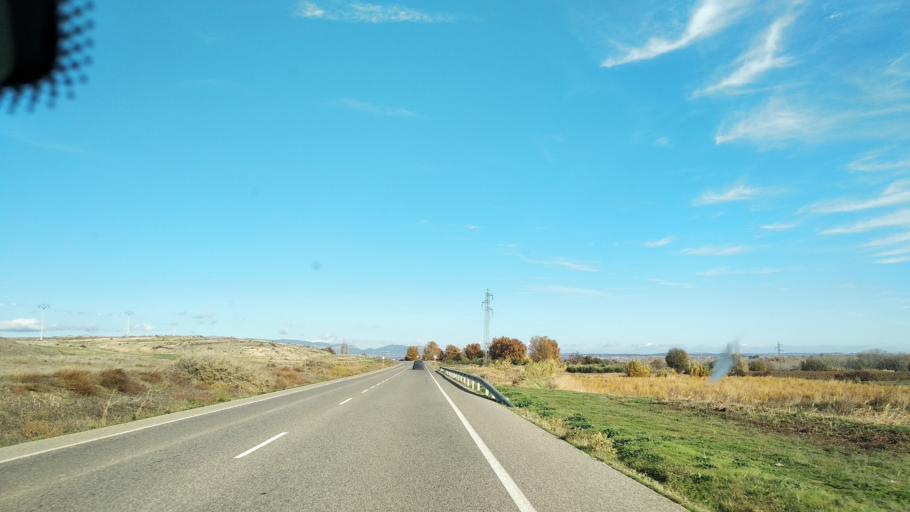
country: ES
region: Catalonia
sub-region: Provincia de Lleida
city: Termens
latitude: 41.7425
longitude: 0.7583
